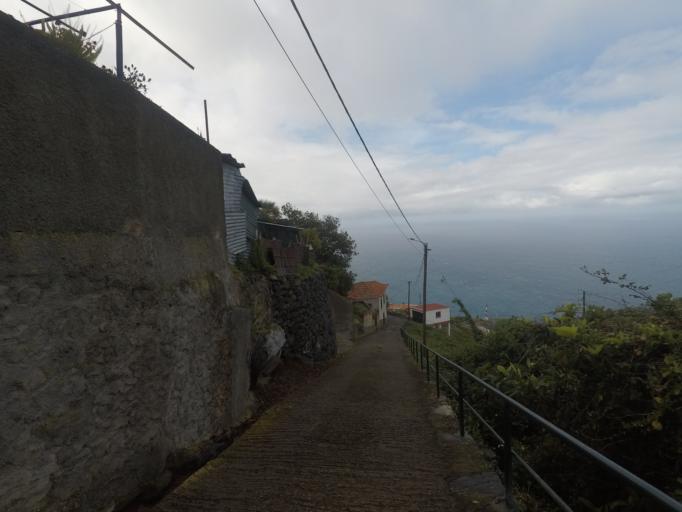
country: PT
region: Madeira
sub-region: Calheta
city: Faja da Ovelha
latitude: 32.7743
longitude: -17.2361
